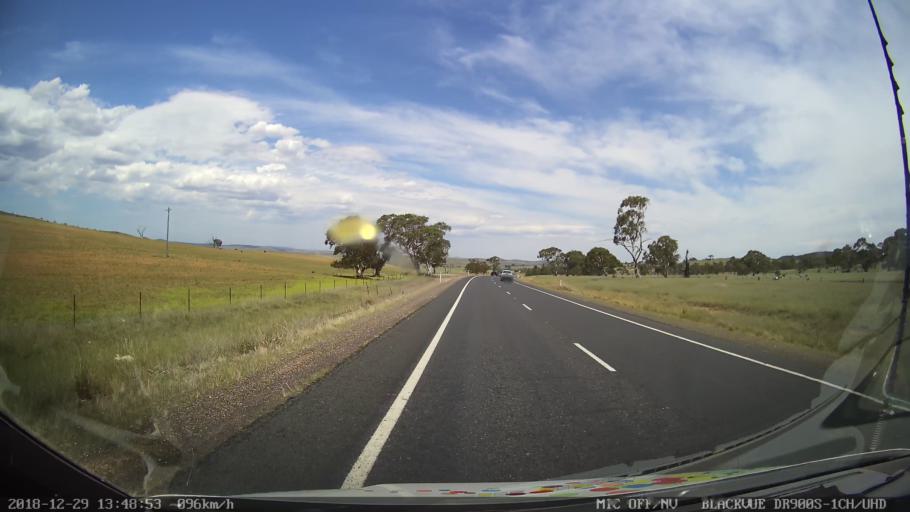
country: AU
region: New South Wales
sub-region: Cooma-Monaro
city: Cooma
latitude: -36.1464
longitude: 149.1498
